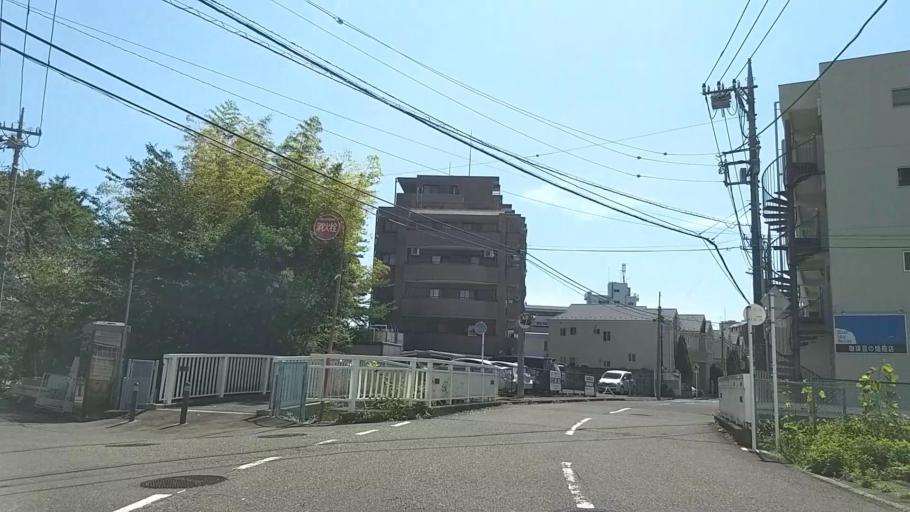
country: JP
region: Tokyo
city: Chofugaoka
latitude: 35.5607
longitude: 139.5610
